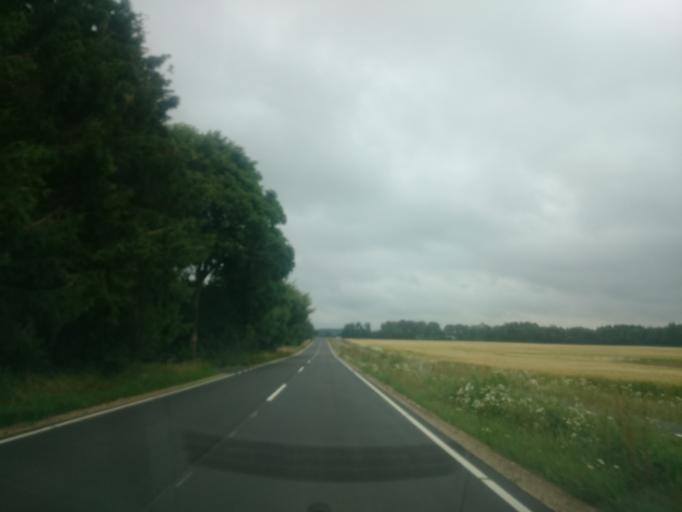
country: DK
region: South Denmark
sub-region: Billund Kommune
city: Billund
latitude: 55.7014
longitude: 9.0058
